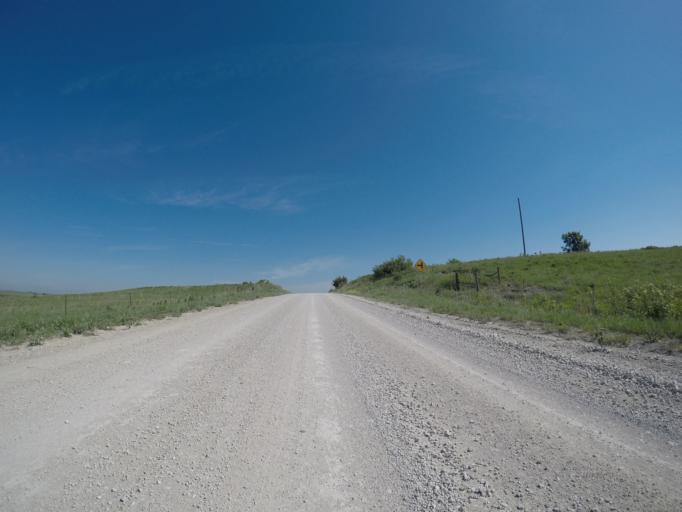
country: US
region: Kansas
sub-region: Wabaunsee County
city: Alma
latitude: 38.9772
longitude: -96.1140
